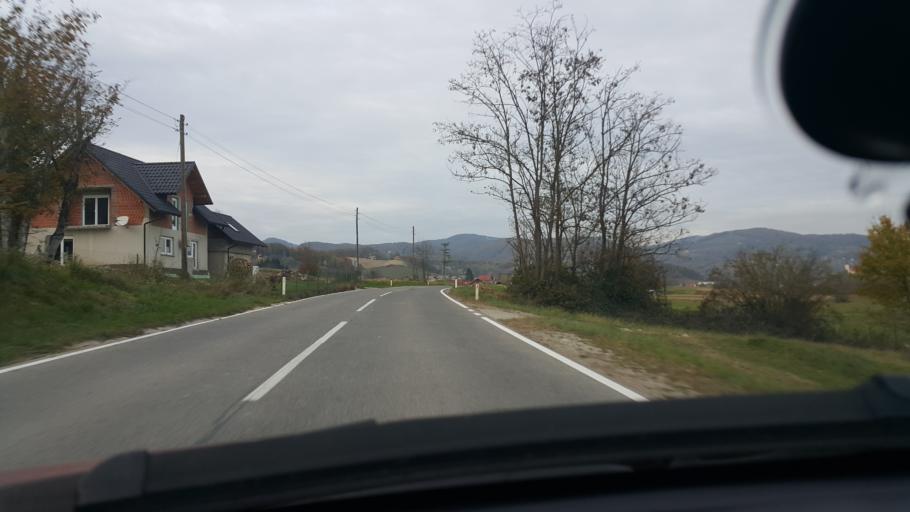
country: SI
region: Bistrica ob Sotli
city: Bistrica ob Sotli
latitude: 45.9962
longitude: 15.6943
